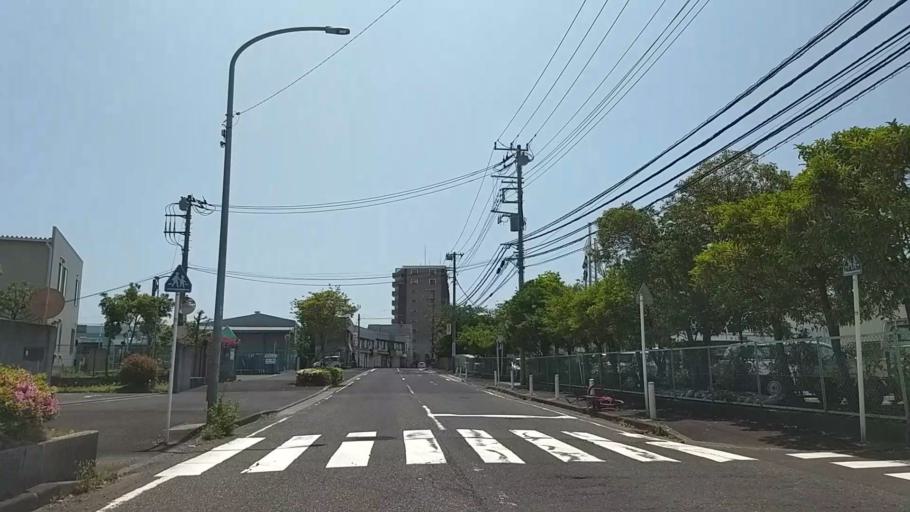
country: JP
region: Kanagawa
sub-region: Kawasaki-shi
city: Kawasaki
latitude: 35.5038
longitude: 139.7036
